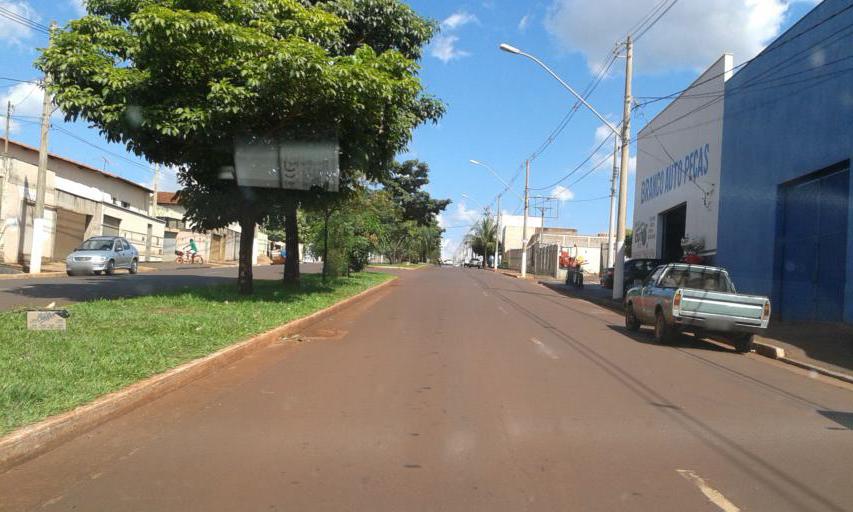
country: BR
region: Minas Gerais
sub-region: Ituiutaba
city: Ituiutaba
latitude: -18.9710
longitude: -49.4871
